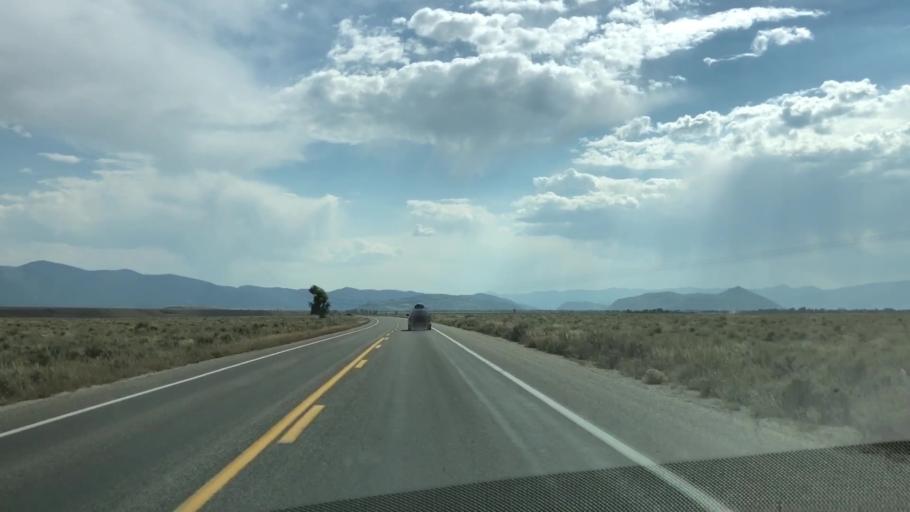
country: US
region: Wyoming
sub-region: Teton County
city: Jackson
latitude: 43.6232
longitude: -110.7212
